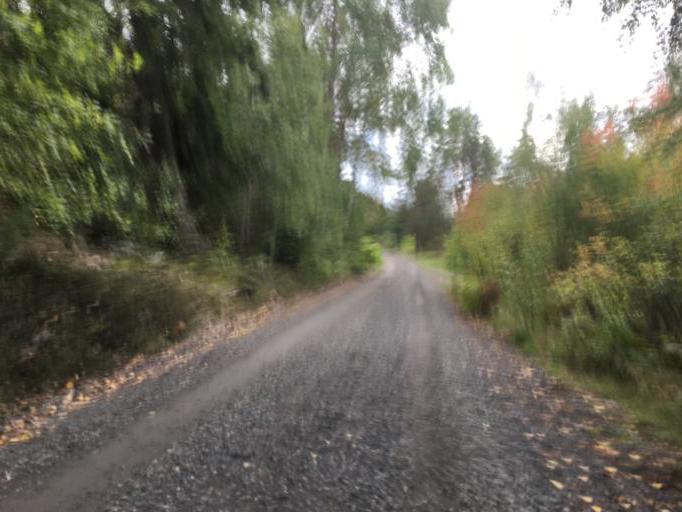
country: SE
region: Soedermanland
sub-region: Eskilstuna Kommun
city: Arla
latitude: 59.4542
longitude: 16.6813
